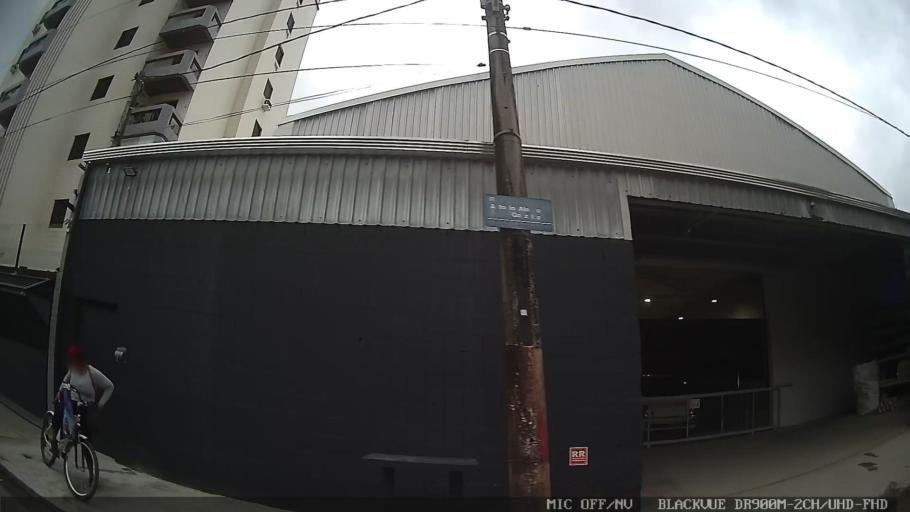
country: BR
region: Sao Paulo
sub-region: Guaruja
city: Guaruja
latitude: -24.0052
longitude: -46.2732
